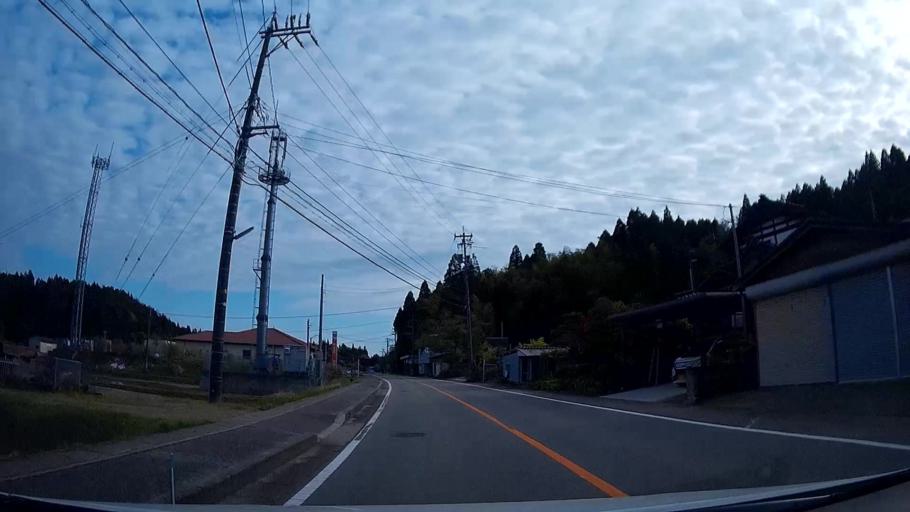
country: JP
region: Ishikawa
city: Nanao
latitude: 37.1317
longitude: 136.9985
